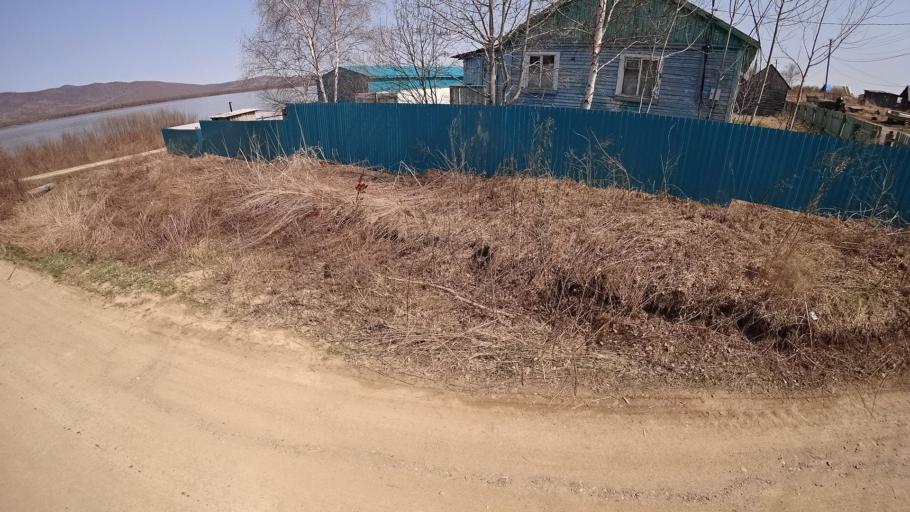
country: RU
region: Khabarovsk Krai
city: Selikhino
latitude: 50.6686
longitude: 137.4010
